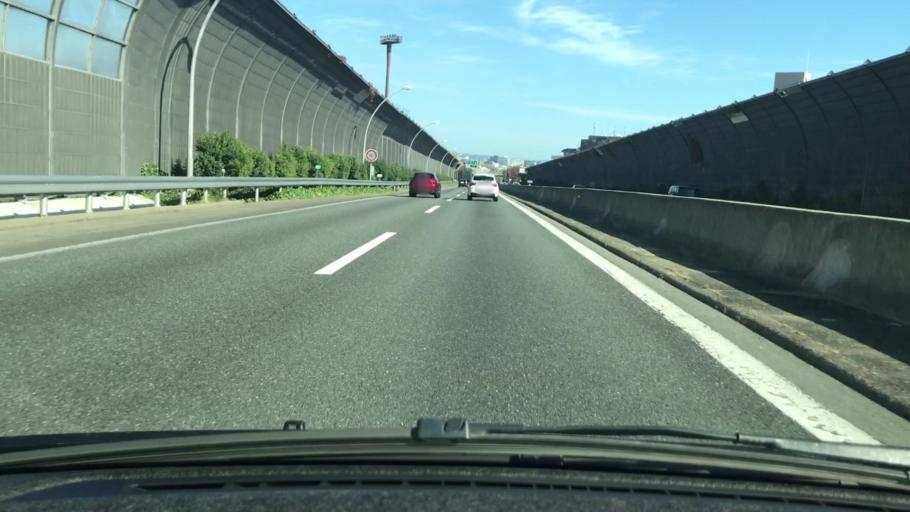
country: JP
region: Osaka
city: Suita
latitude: 34.7781
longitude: 135.5221
